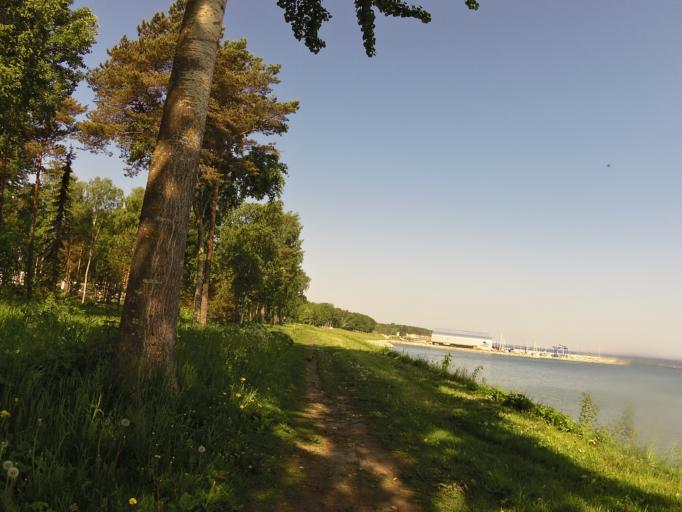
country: EE
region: Harju
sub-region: Harku vald
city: Tabasalu
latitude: 59.4472
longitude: 24.6127
